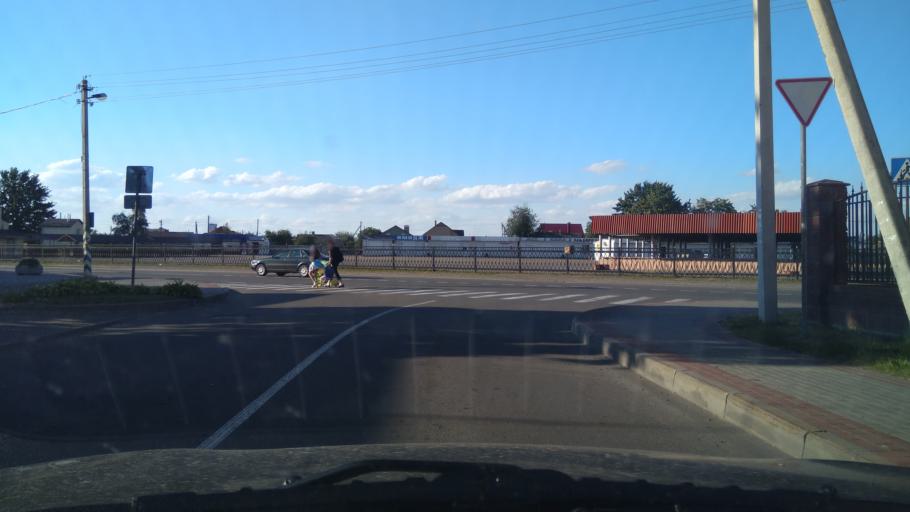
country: BY
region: Brest
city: Byaroza
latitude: 52.5403
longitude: 24.9780
